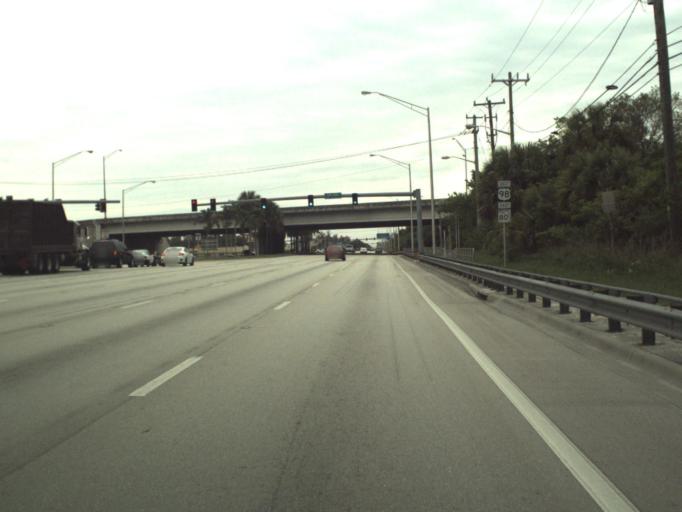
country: US
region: Florida
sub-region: Palm Beach County
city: Lake Belvedere Estates
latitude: 26.6792
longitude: -80.1683
